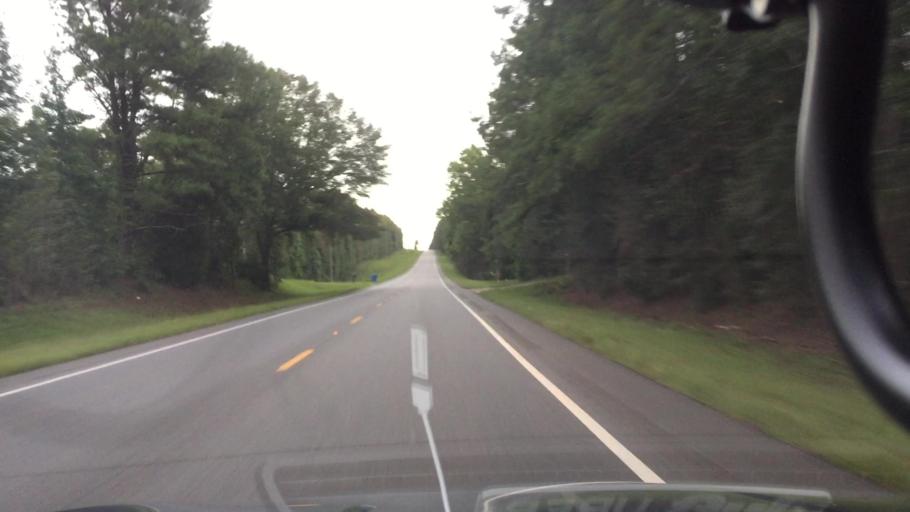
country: US
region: Alabama
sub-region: Coffee County
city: New Brockton
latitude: 31.5260
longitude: -85.9177
